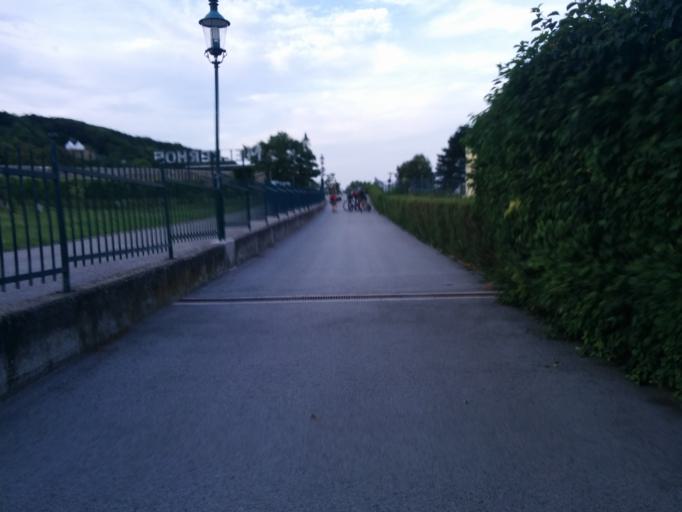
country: AT
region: Lower Austria
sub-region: Politischer Bezirk Modling
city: Gumpoldskirchen
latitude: 48.0468
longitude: 16.2763
